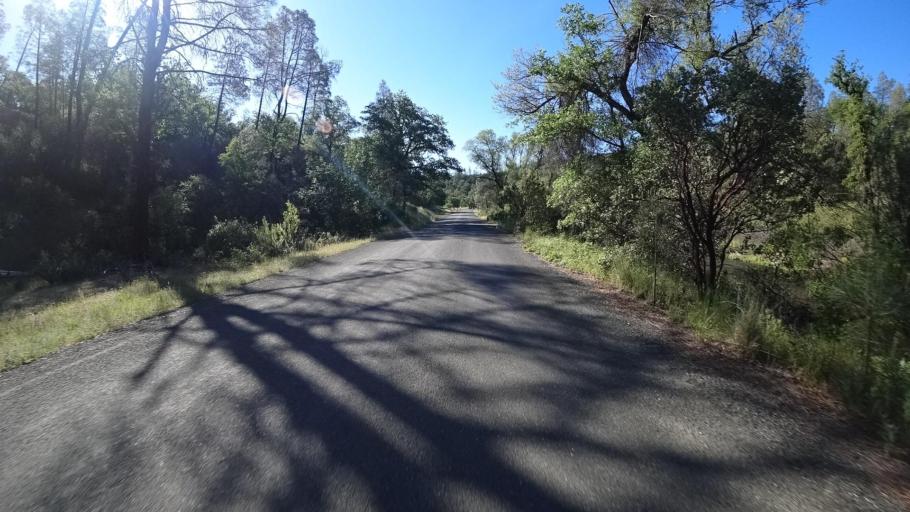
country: US
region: California
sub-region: Lake County
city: Upper Lake
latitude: 39.4165
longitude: -122.9765
